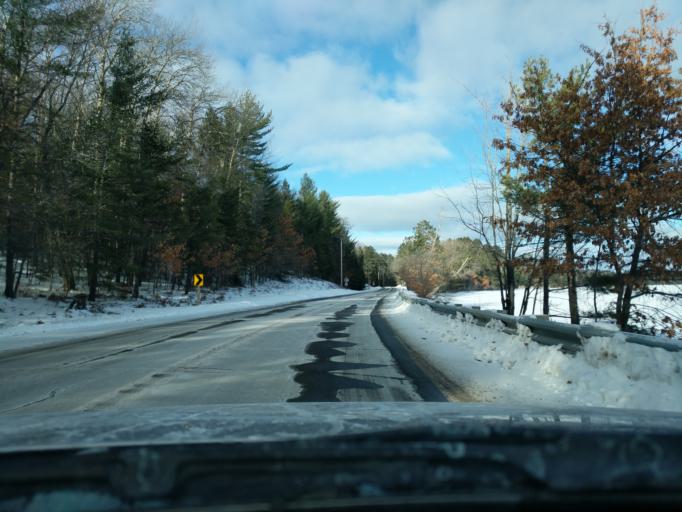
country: US
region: Wisconsin
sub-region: Vilas County
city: Eagle River
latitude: 45.7753
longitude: -89.0756
